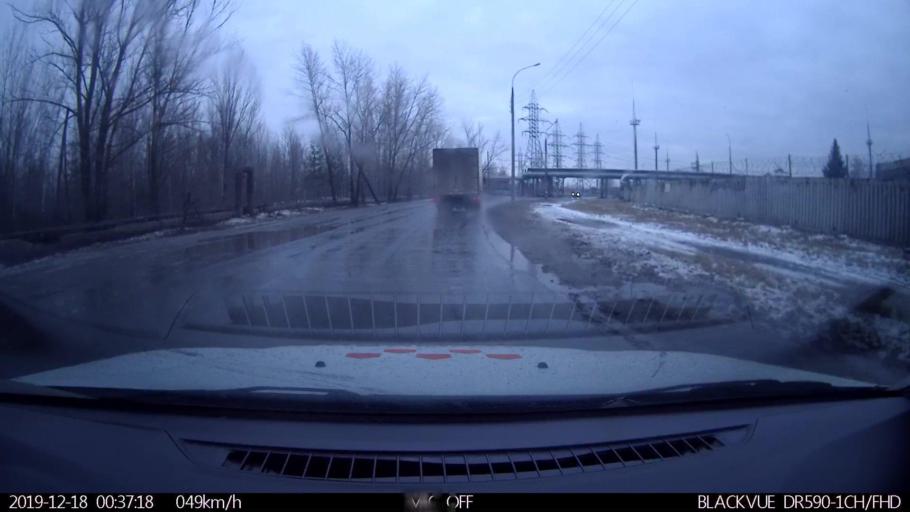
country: RU
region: Nizjnij Novgorod
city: Neklyudovo
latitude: 56.3536
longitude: 43.8954
